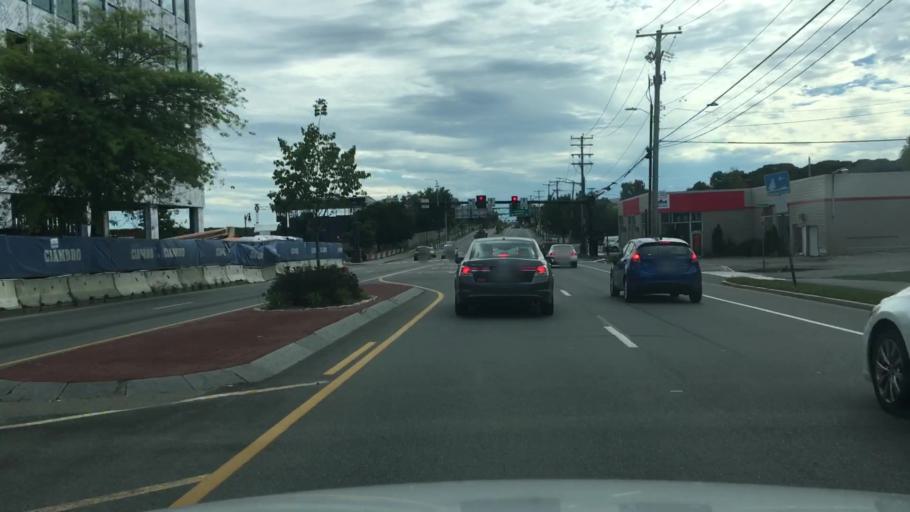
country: US
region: Maine
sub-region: Penobscot County
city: Bangor
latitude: 44.7961
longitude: -68.7741
